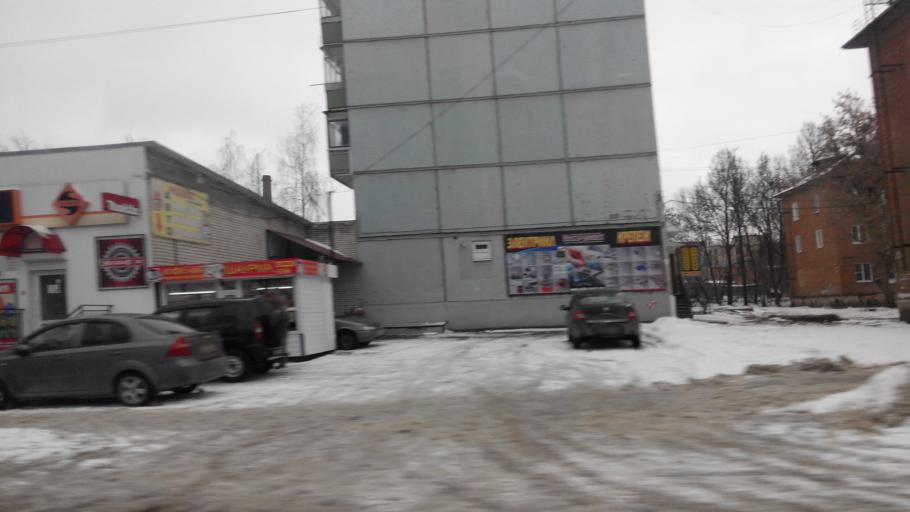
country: RU
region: Tula
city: Uzlovaya
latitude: 53.9680
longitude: 38.1658
